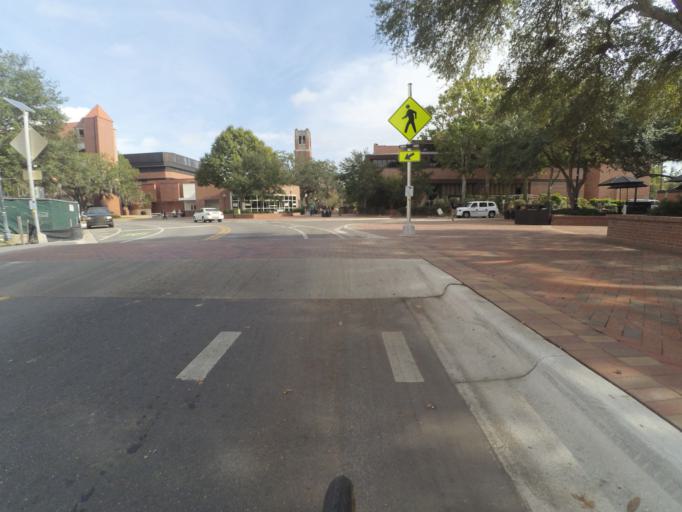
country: US
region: Florida
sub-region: Alachua County
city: Gainesville
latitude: 29.6486
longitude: -82.3452
